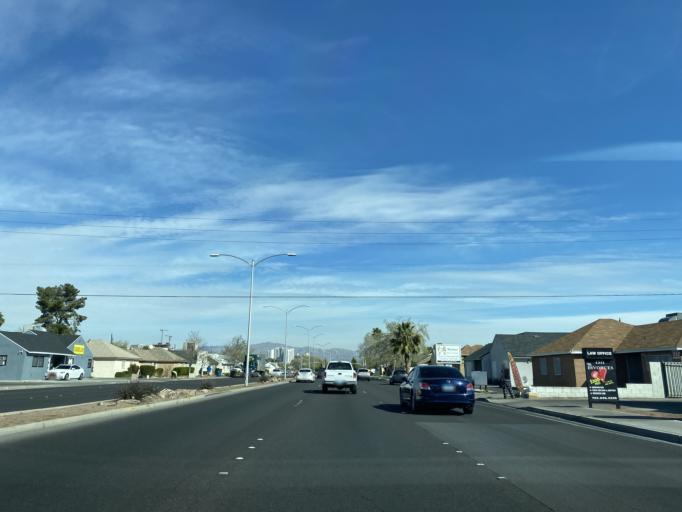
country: US
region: Nevada
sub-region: Clark County
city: Las Vegas
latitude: 36.1523
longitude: -115.1369
